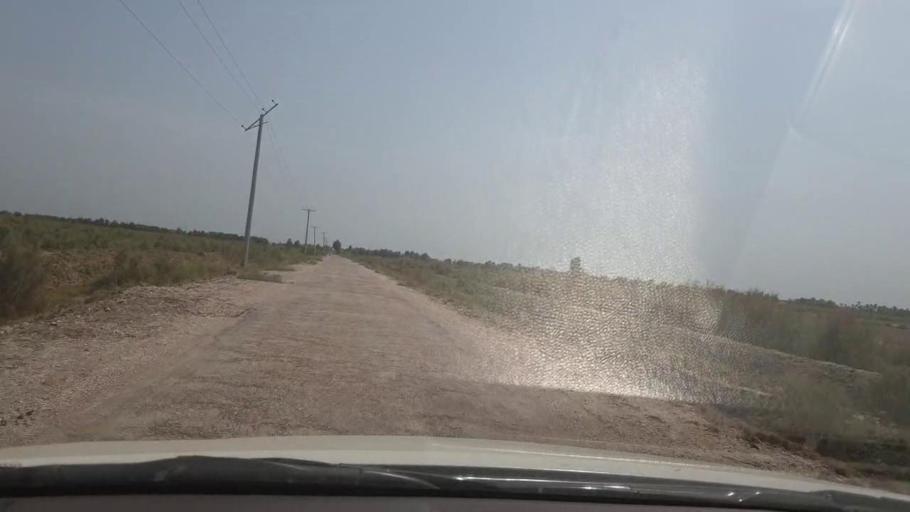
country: PK
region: Sindh
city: Garhi Yasin
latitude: 27.9822
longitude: 68.5024
